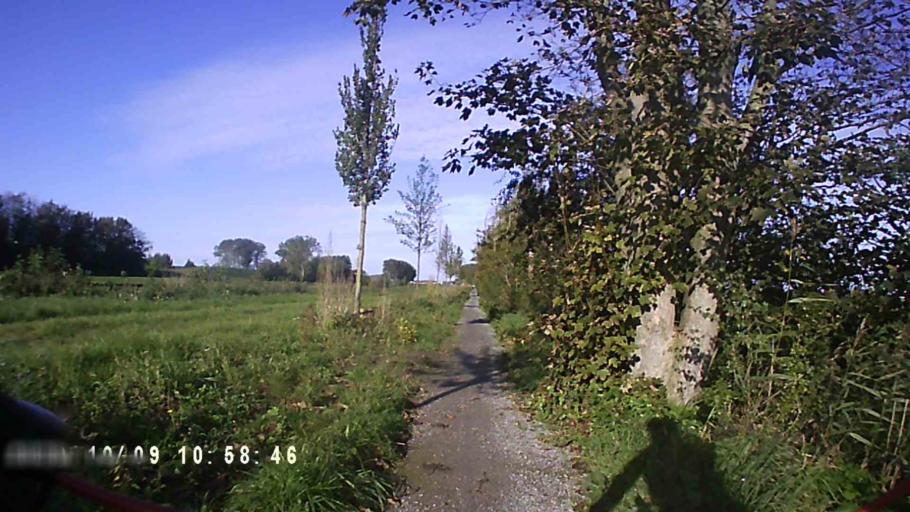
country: NL
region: Groningen
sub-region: Gemeente Zuidhorn
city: Aduard
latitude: 53.2556
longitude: 6.5159
